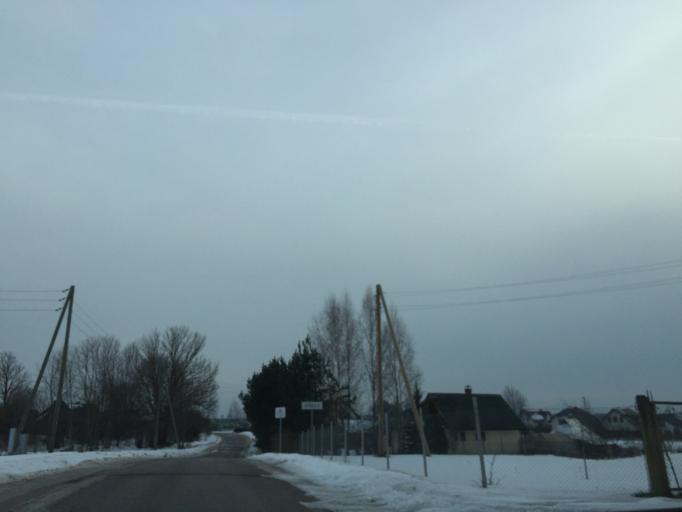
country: LV
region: Ikskile
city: Ikskile
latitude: 56.8420
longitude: 24.4724
